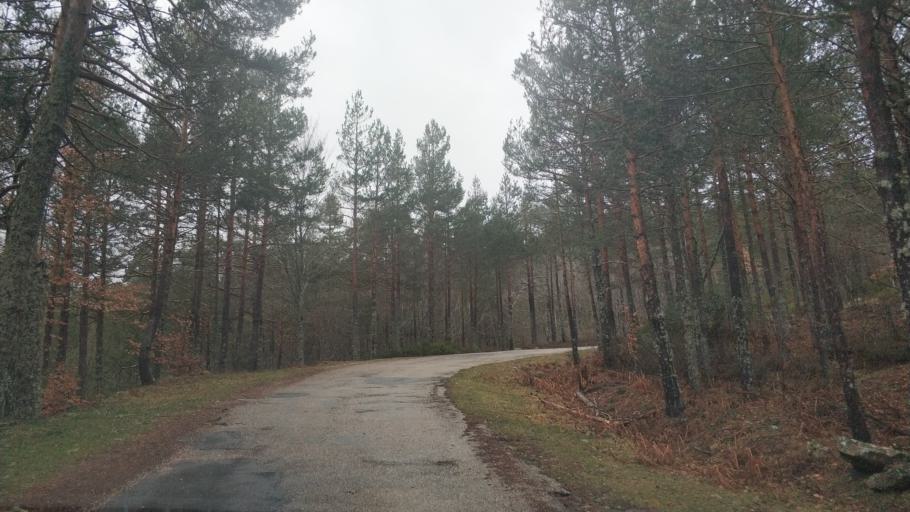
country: ES
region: Castille and Leon
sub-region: Provincia de Burgos
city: Neila
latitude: 42.0444
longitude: -3.0176
